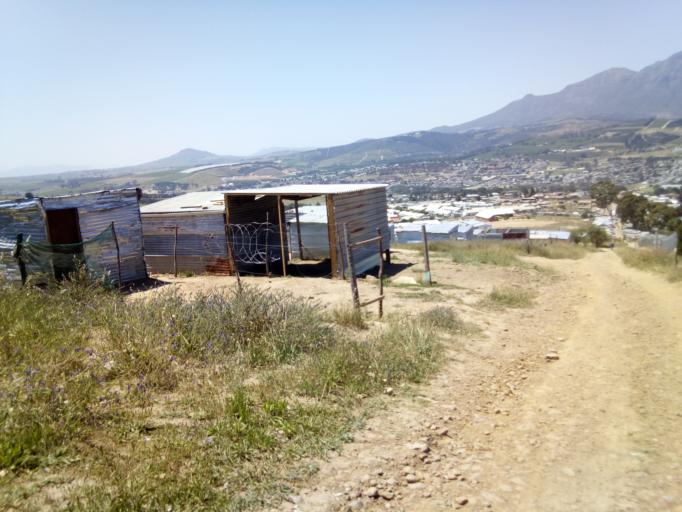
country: ZA
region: Western Cape
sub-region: Cape Winelands District Municipality
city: Stellenbosch
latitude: -33.9250
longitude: 18.8393
